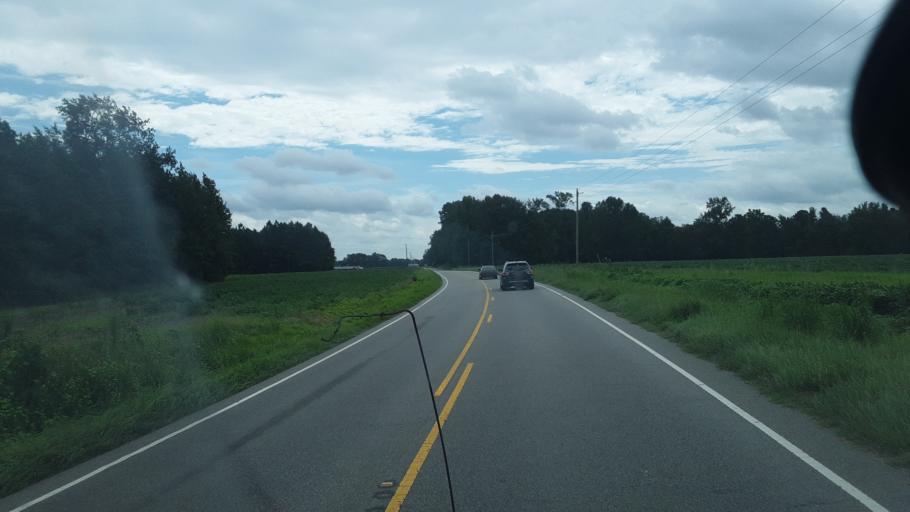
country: US
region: North Carolina
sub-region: Robeson County
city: Rowland
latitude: 34.6064
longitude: -79.3317
